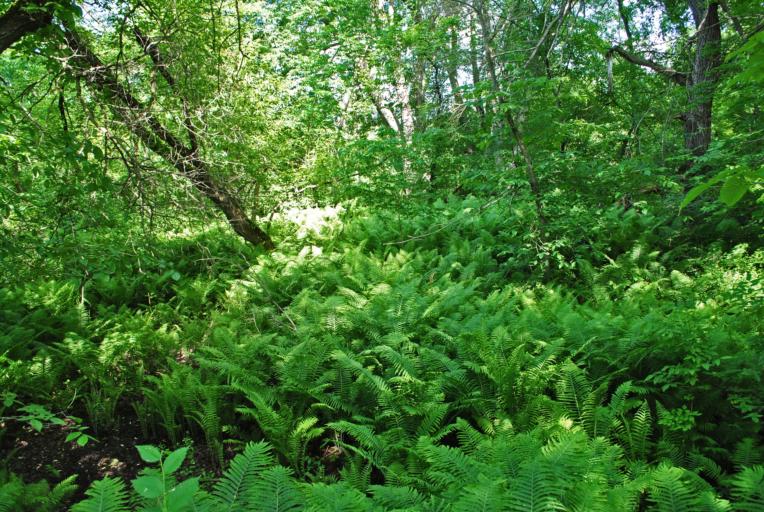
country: US
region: Wisconsin
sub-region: Dunn County
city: Menomonie
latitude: 44.8209
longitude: -91.9483
